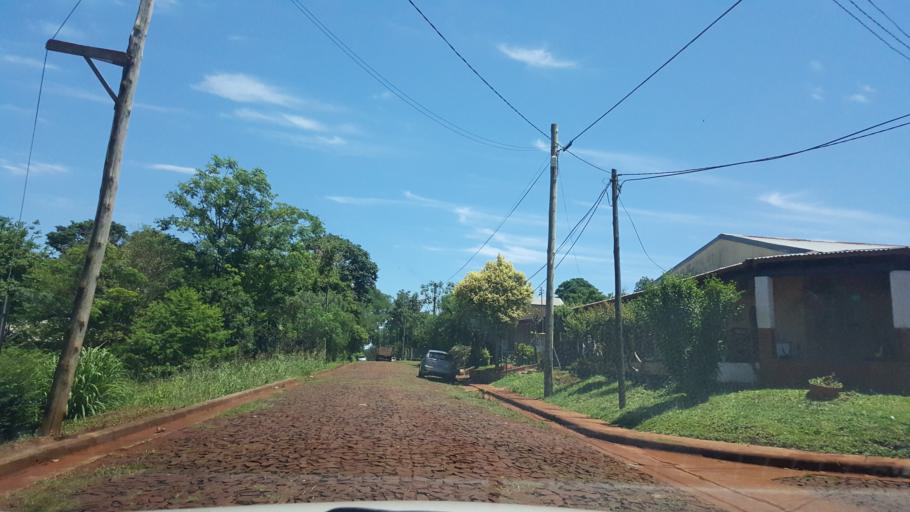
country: AR
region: Misiones
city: Capiovi
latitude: -26.9359
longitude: -55.0594
